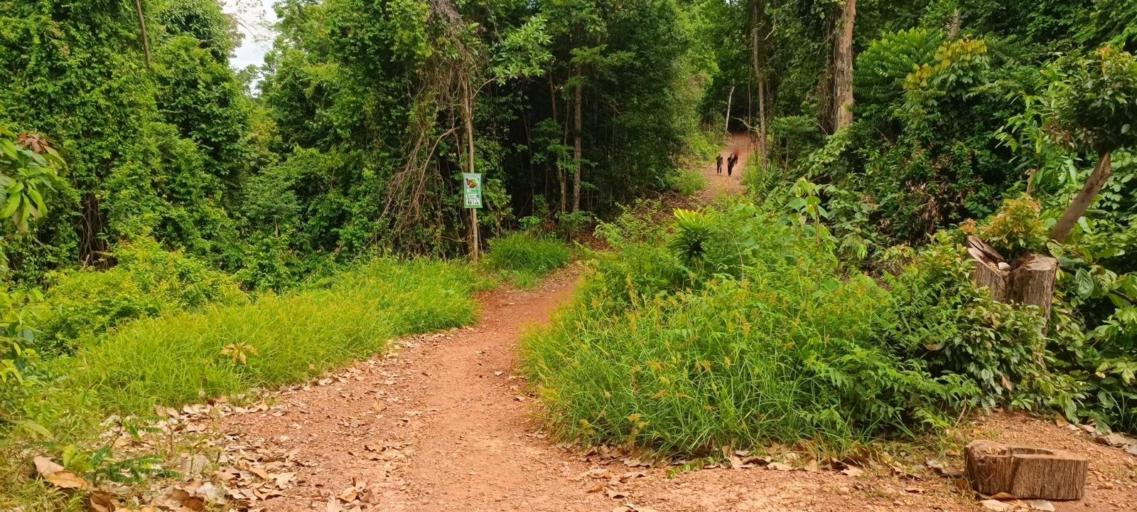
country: MY
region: Kedah
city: Sungai Petani
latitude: 5.6050
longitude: 100.4556
